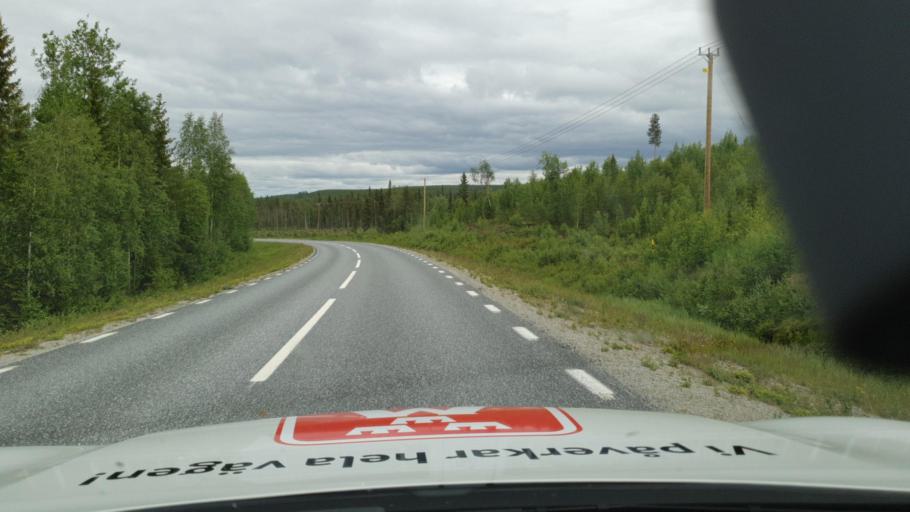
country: SE
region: Vaesterbotten
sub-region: Asele Kommun
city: Insjon
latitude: 64.2888
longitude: 17.6405
